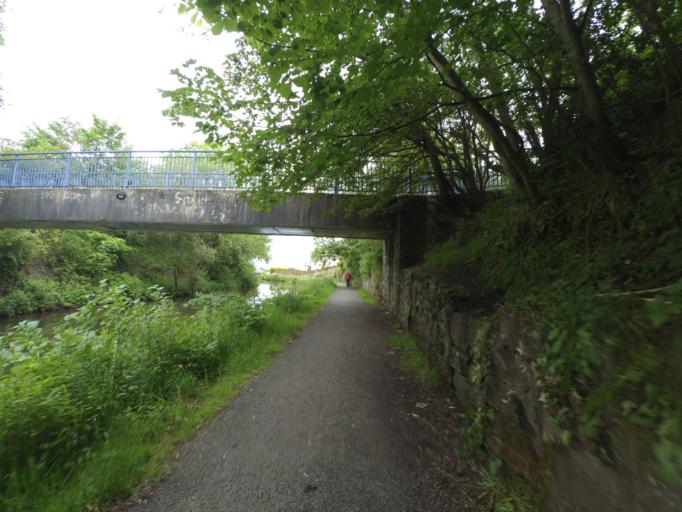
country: GB
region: Scotland
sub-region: Falkirk
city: Polmont
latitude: 55.9837
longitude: -3.7180
